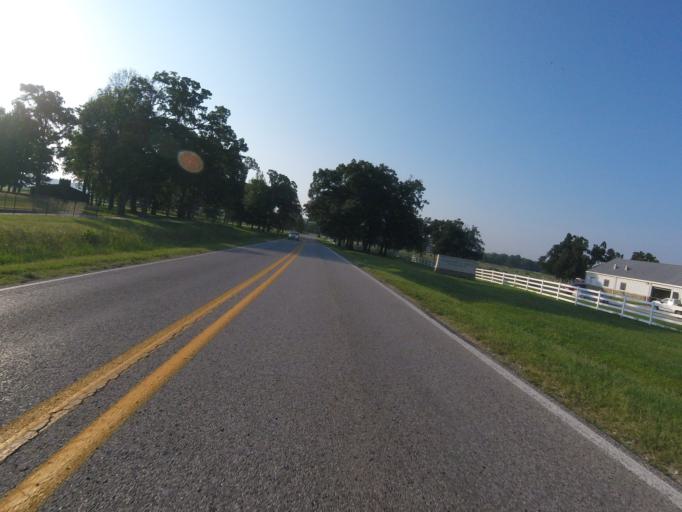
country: US
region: Arkansas
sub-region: Washington County
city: Fayetteville
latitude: 36.0949
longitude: -94.1770
